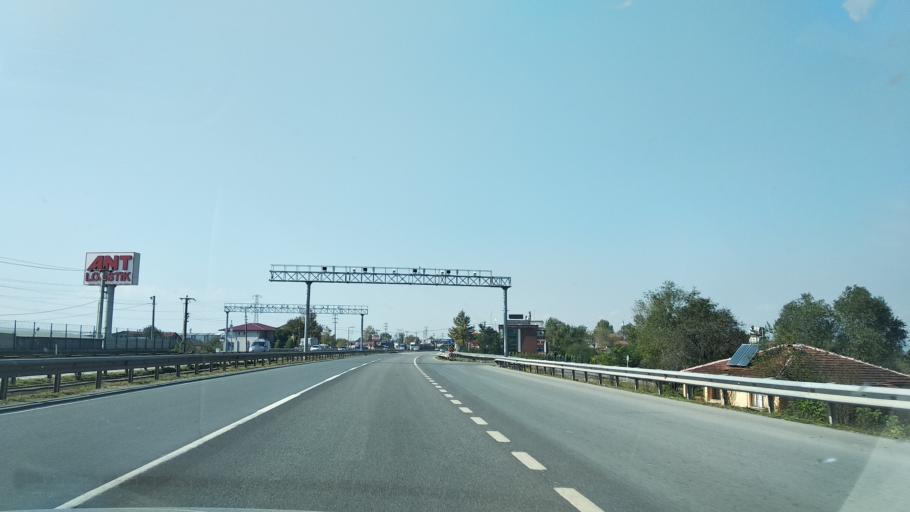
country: TR
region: Kocaeli
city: Derbent
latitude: 40.7296
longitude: 30.1404
